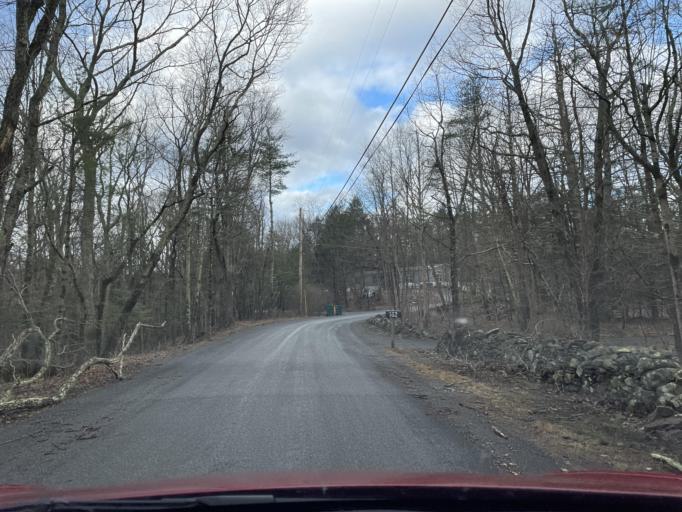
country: US
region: New York
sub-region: Ulster County
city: Manorville
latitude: 42.0807
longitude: -74.0486
